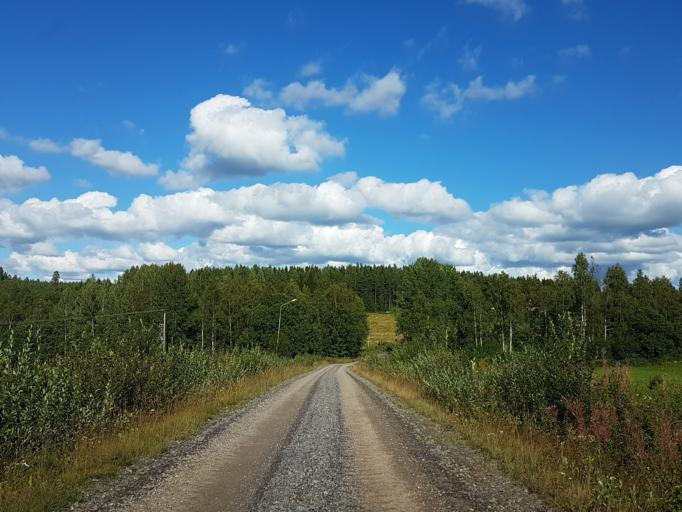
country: SE
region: Vaesterbotten
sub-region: Skelleftea Kommun
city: Burtraesk
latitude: 64.2917
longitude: 20.4552
